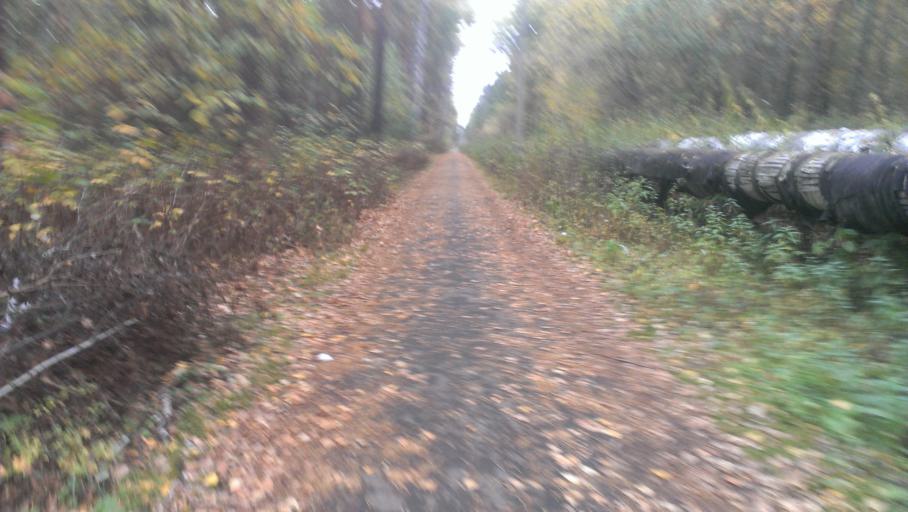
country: RU
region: Altai Krai
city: Yuzhnyy
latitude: 53.2604
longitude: 83.6884
